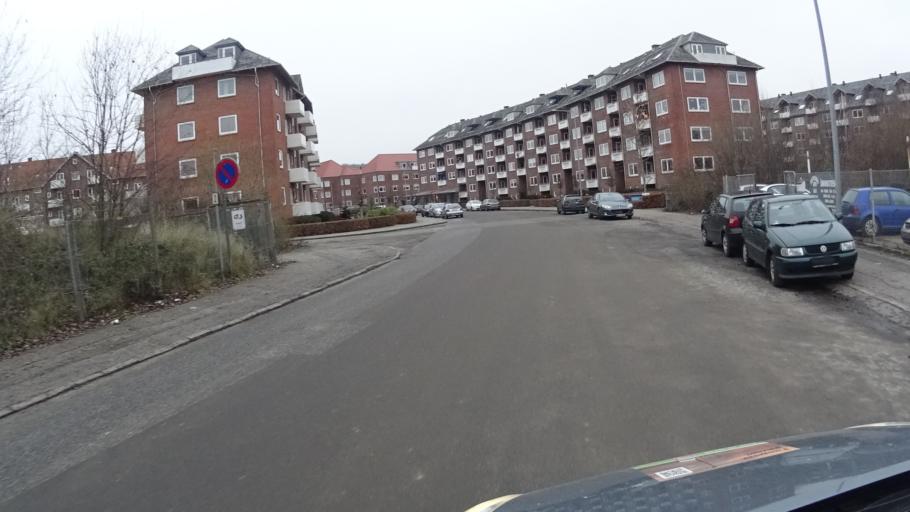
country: DK
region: South Denmark
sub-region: Vejle Kommune
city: Vejle
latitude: 55.7089
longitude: 9.5486
